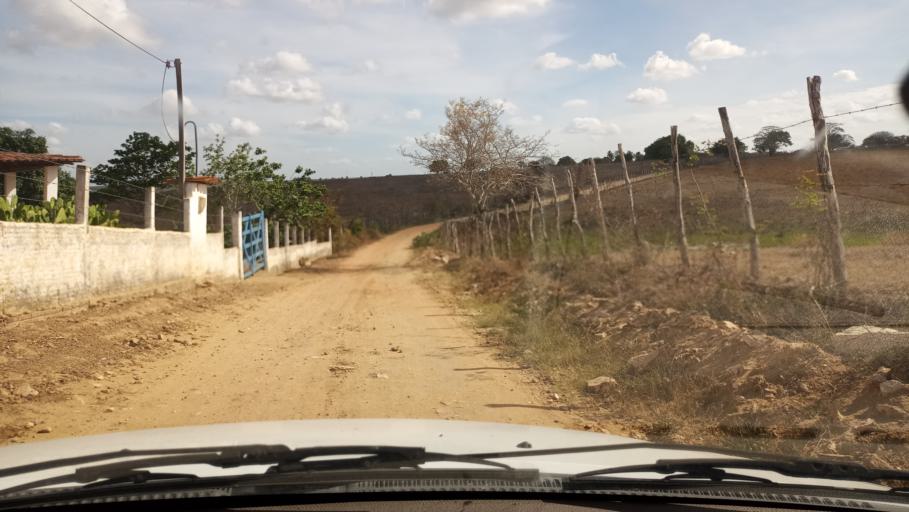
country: BR
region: Rio Grande do Norte
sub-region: Goianinha
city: Goianinha
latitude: -6.3128
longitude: -35.3067
